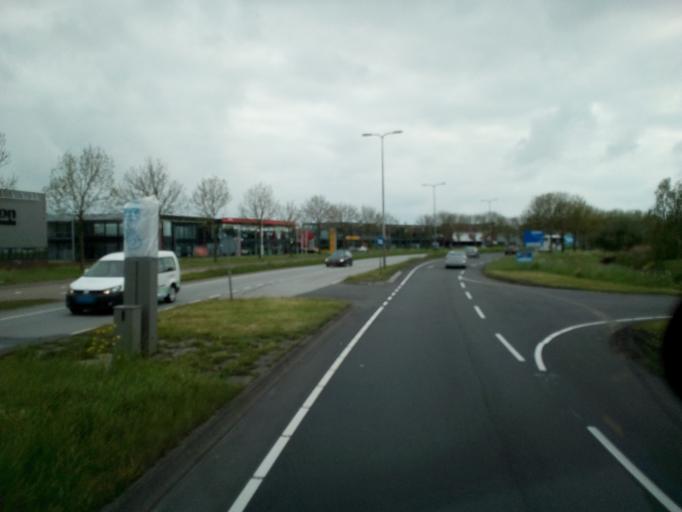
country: NL
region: South Holland
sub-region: Gemeente Alphen aan den Rijn
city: Alphen aan den Rijn
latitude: 52.1279
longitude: 4.6291
